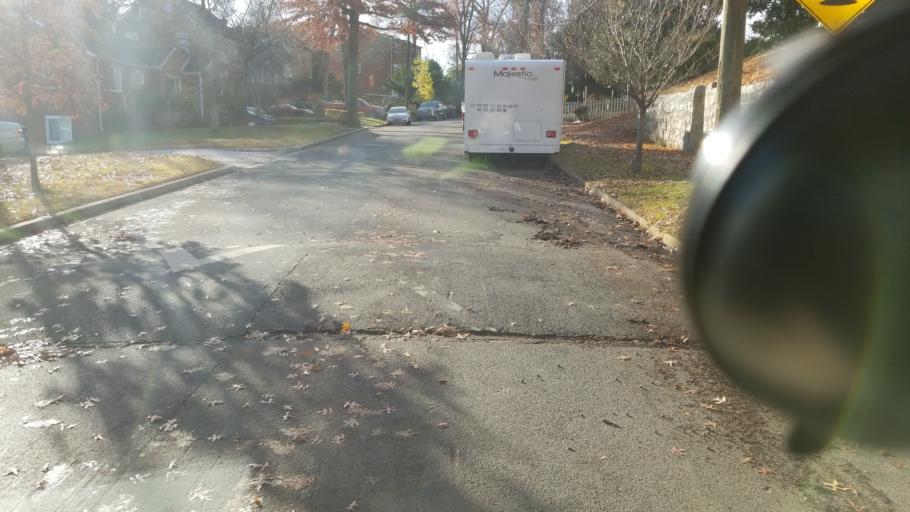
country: US
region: Maryland
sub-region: Prince George's County
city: Silver Hill
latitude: 38.8623
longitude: -76.9536
